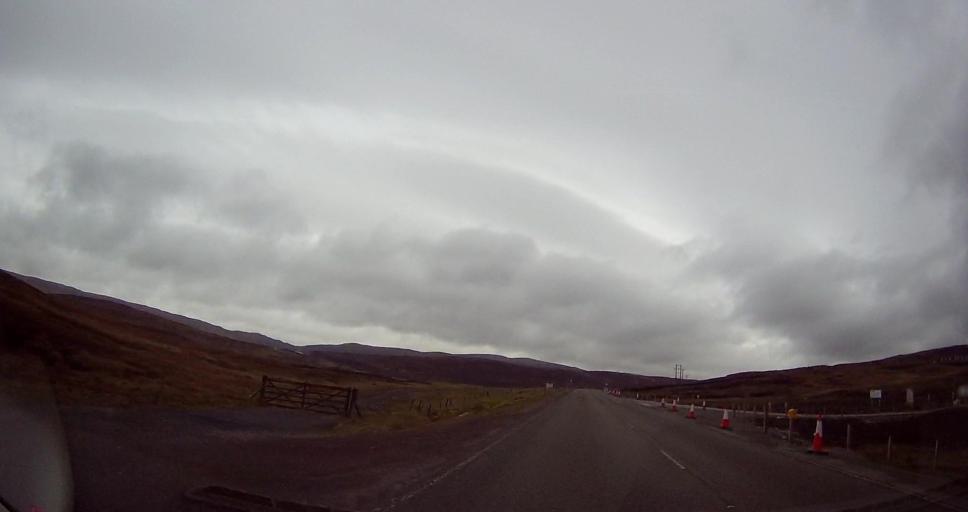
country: GB
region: Scotland
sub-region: Shetland Islands
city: Lerwick
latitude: 60.2717
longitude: -1.2378
